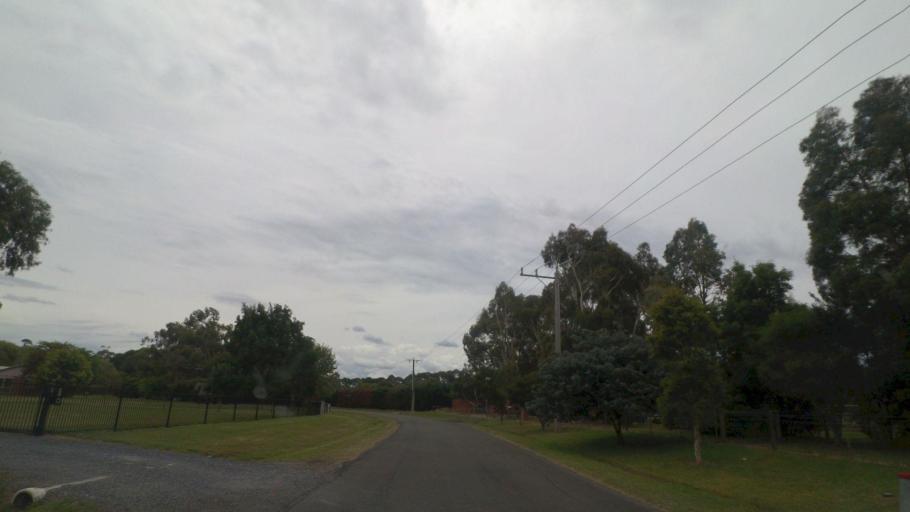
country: AU
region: Victoria
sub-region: Knox
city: The Basin
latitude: -37.8405
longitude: 145.3162
